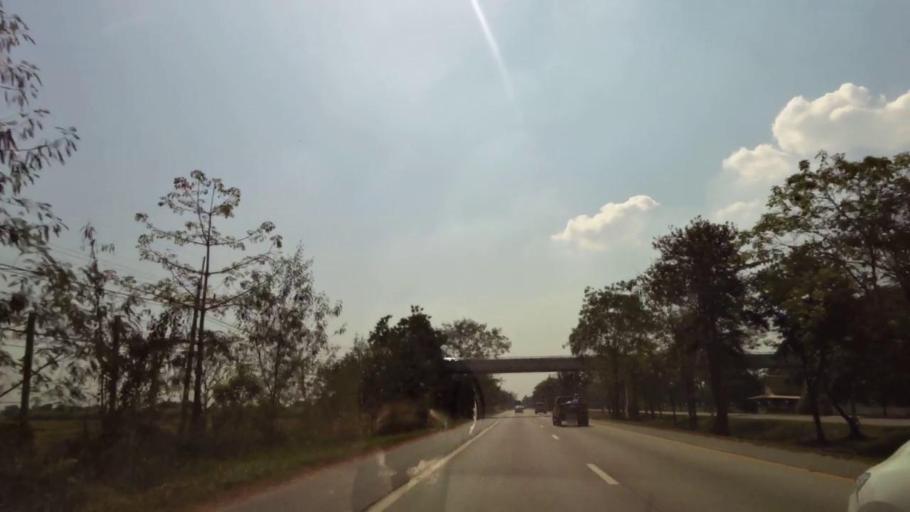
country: TH
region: Phichit
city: Wachira Barami
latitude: 16.5509
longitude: 100.1467
